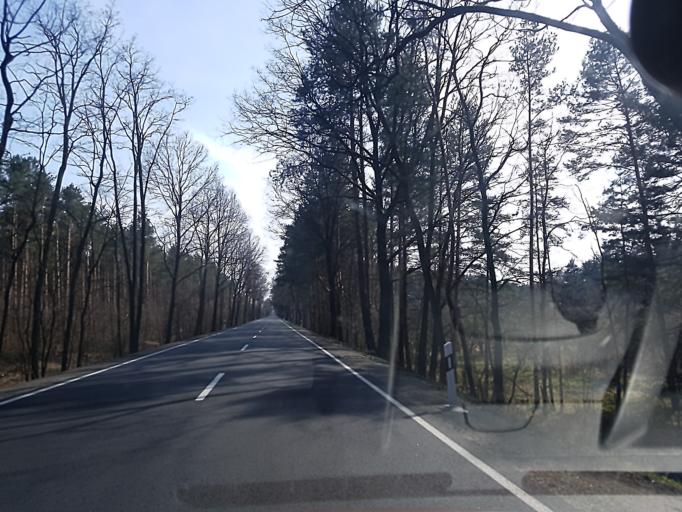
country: DE
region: Brandenburg
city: Bronkow
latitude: 51.6942
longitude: 13.9183
